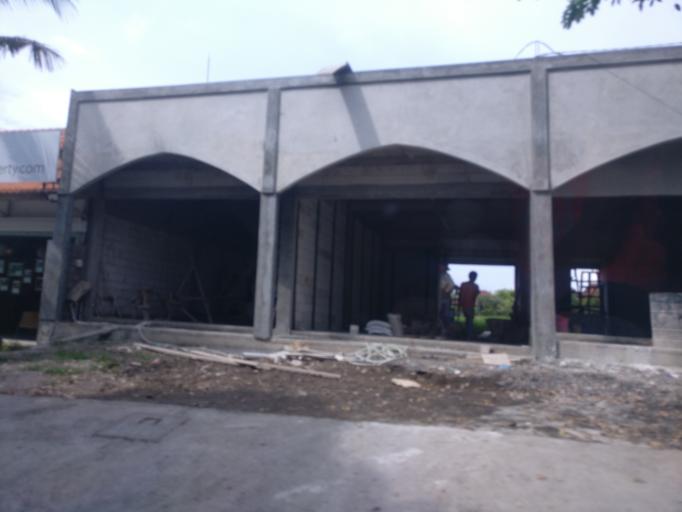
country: ID
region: Bali
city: Banjar Gunungpande
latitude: -8.6607
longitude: 115.1445
